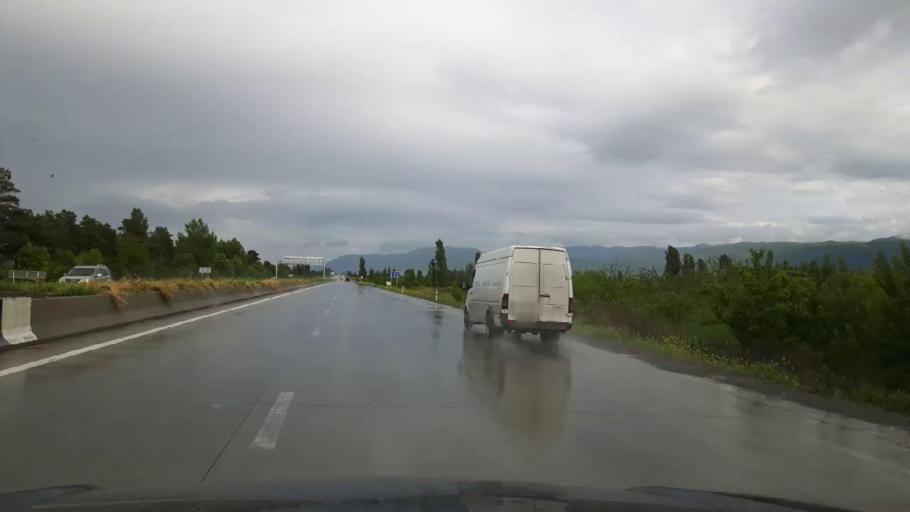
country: GE
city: Agara
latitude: 42.0471
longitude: 43.9166
